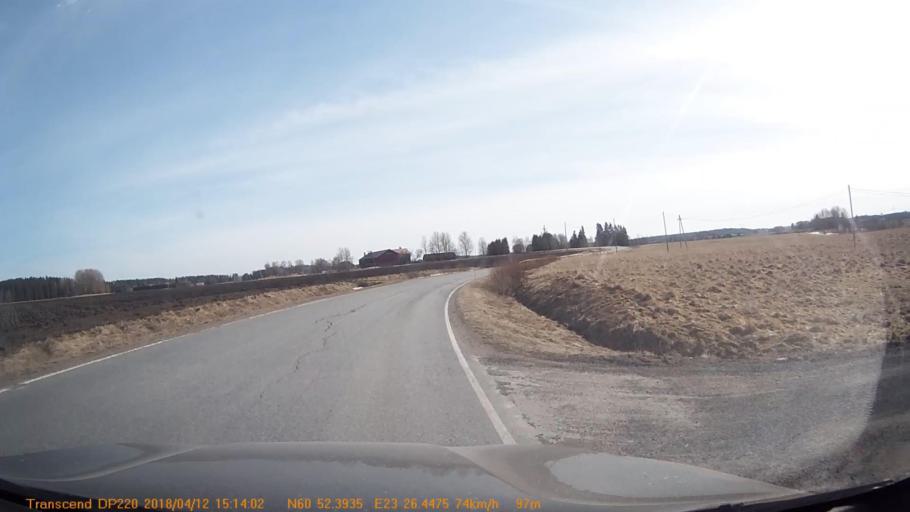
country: FI
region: Haeme
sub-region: Forssa
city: Jokioinen
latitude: 60.8731
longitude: 23.4409
